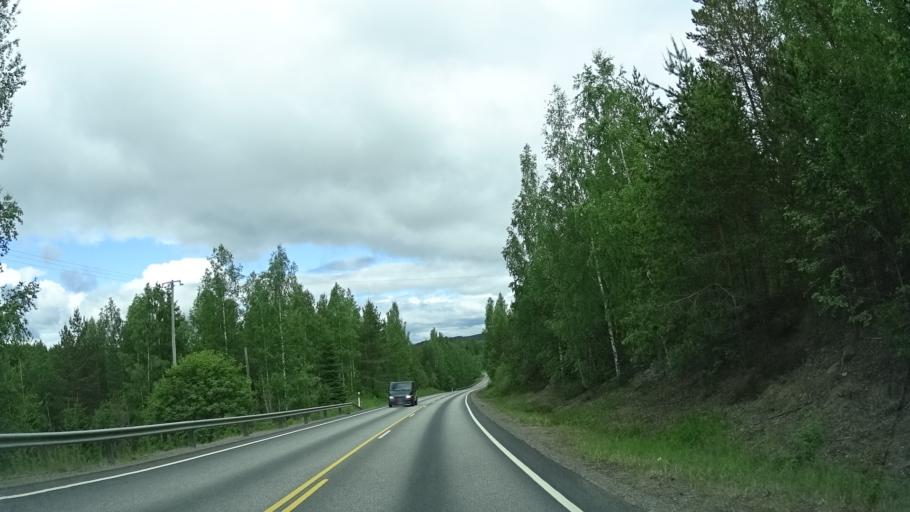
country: FI
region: Central Finland
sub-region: Joutsa
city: Luhanka
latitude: 61.9424
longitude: 25.7041
